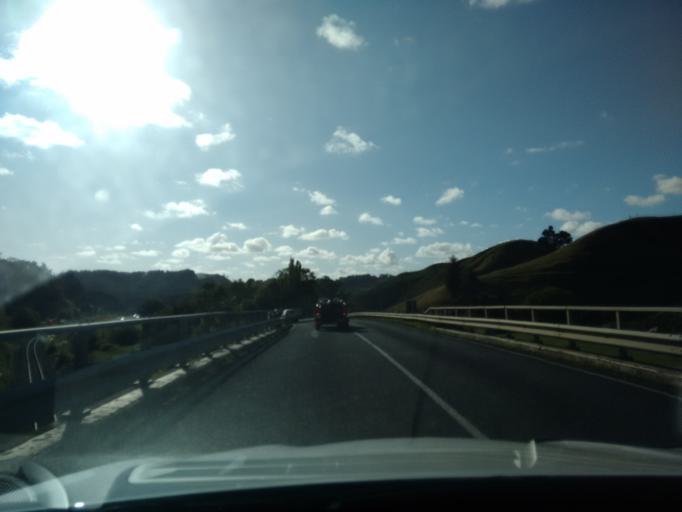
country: NZ
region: Manawatu-Wanganui
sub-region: Wanganui District
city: Wanganui
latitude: -39.8533
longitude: 174.9353
